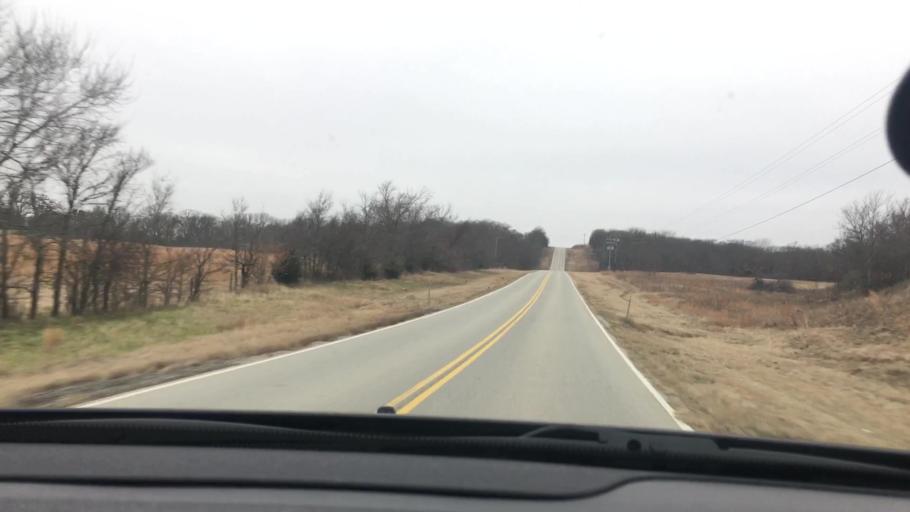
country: US
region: Oklahoma
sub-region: Coal County
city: Coalgate
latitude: 34.5057
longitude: -96.3113
